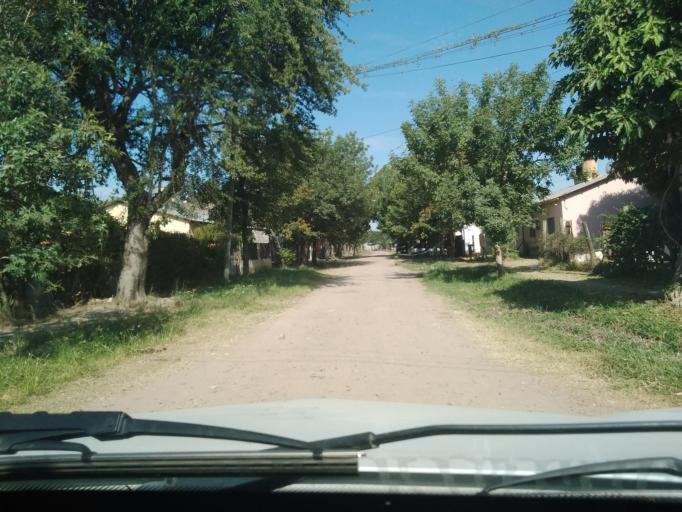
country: AR
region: Corrientes
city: Corrientes
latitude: -27.5109
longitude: -58.8004
